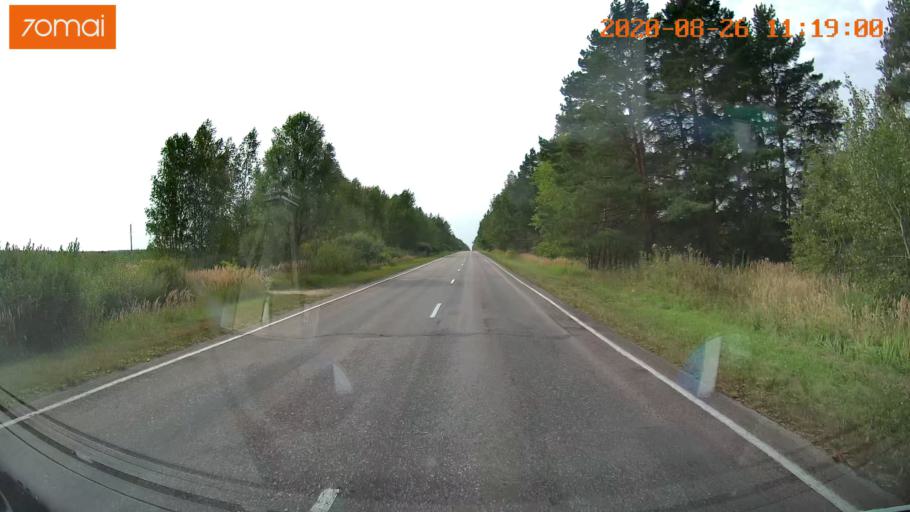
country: RU
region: Rjazan
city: Shilovo
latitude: 54.4040
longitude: 41.0873
